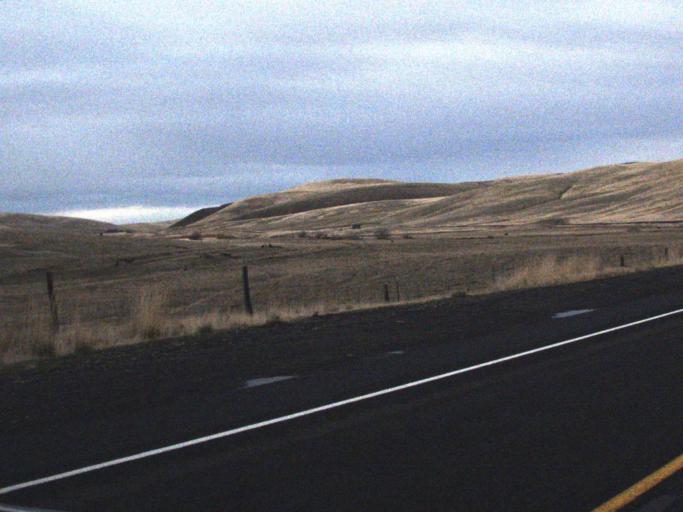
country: US
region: Washington
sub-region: Columbia County
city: Dayton
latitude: 46.5096
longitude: -117.9552
